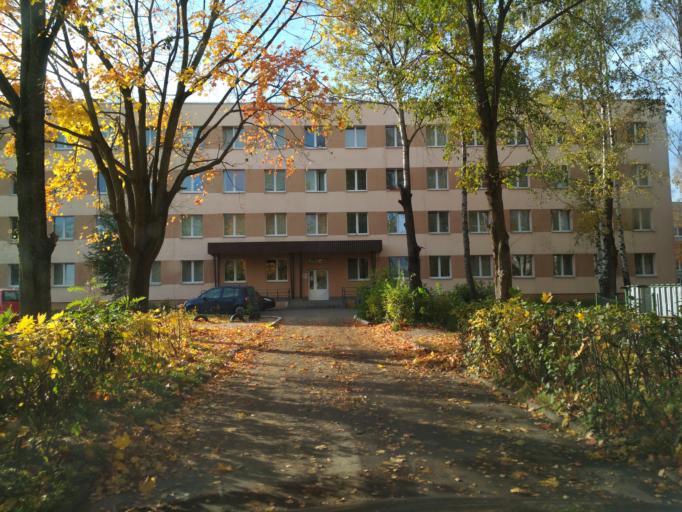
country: BY
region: Minsk
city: Blon'
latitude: 53.5026
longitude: 28.1707
